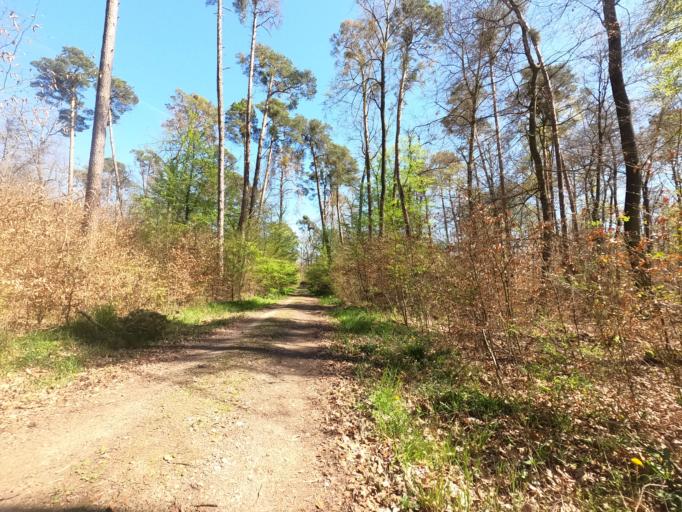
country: DE
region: Hesse
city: Morfelden-Walldorf
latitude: 49.9576
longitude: 8.5920
